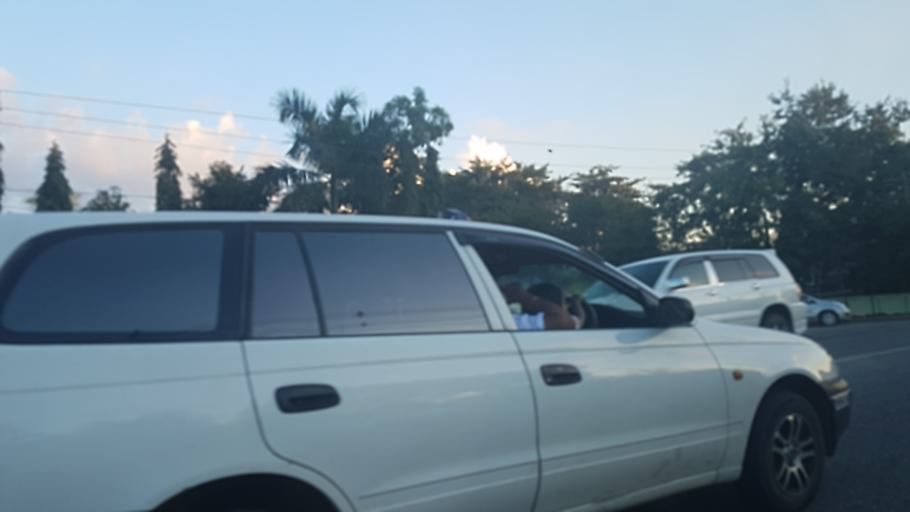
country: MM
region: Yangon
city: Yangon
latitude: 16.8952
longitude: 96.1213
